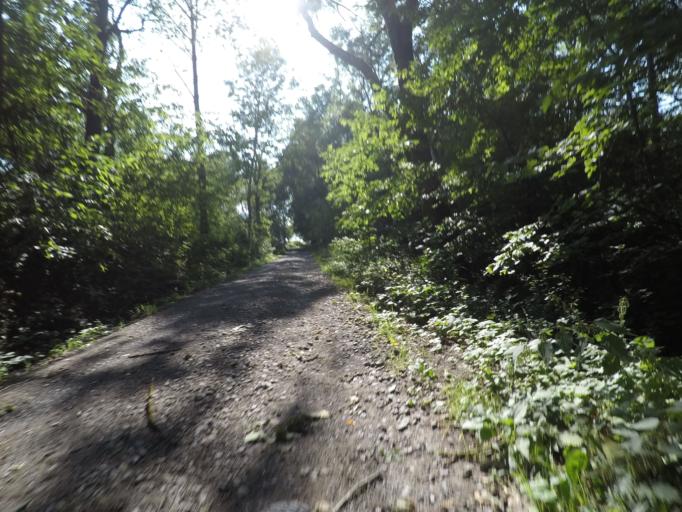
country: DE
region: Baden-Wuerttemberg
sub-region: Regierungsbezirk Stuttgart
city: Weil im Schonbuch
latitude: 48.6361
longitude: 9.0665
